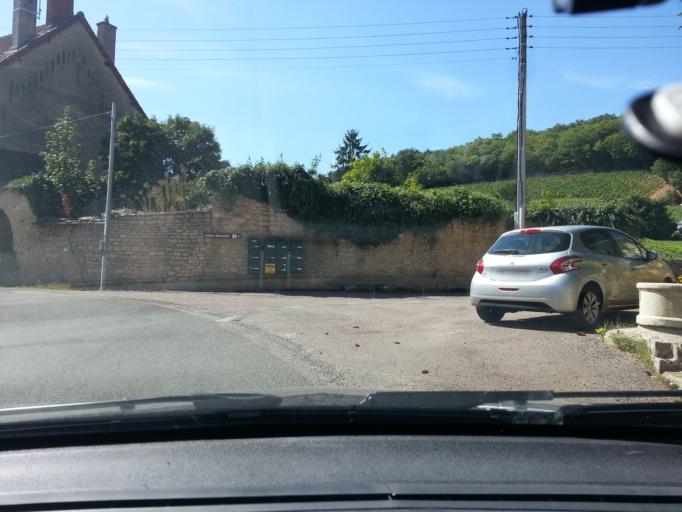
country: FR
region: Bourgogne
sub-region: Departement de Saone-et-Loire
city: Givry
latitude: 46.7793
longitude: 4.7297
